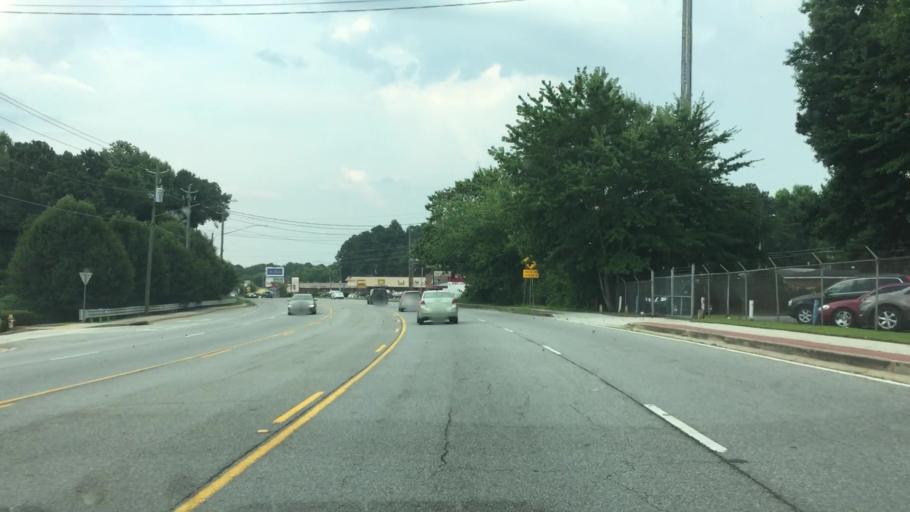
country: US
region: Georgia
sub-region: DeKalb County
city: Belvedere Park
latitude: 33.7626
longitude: -84.2499
